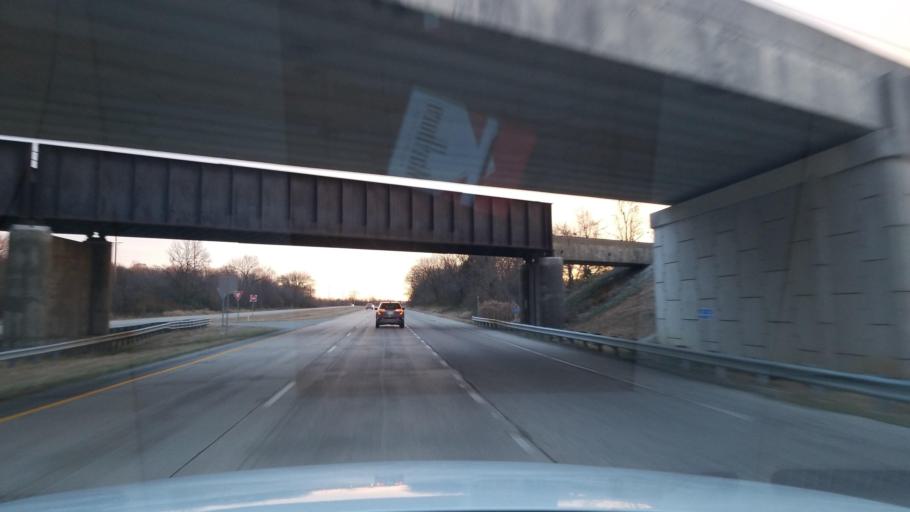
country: US
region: Indiana
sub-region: Posey County
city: Mount Vernon
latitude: 37.9419
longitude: -87.7373
